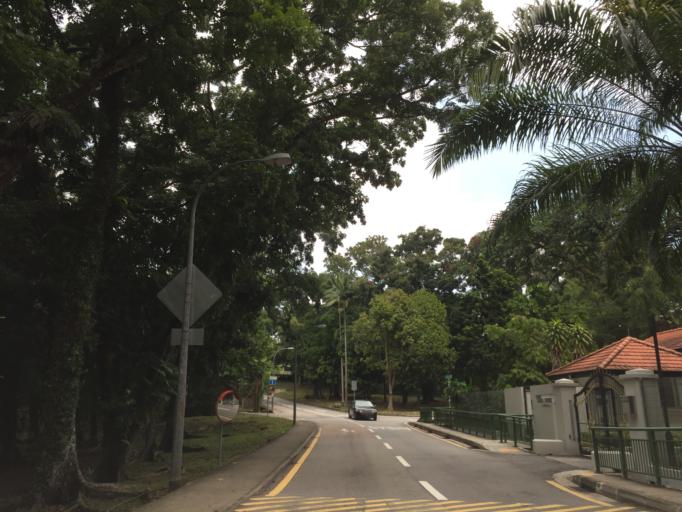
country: SG
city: Singapore
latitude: 1.3068
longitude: 103.8082
